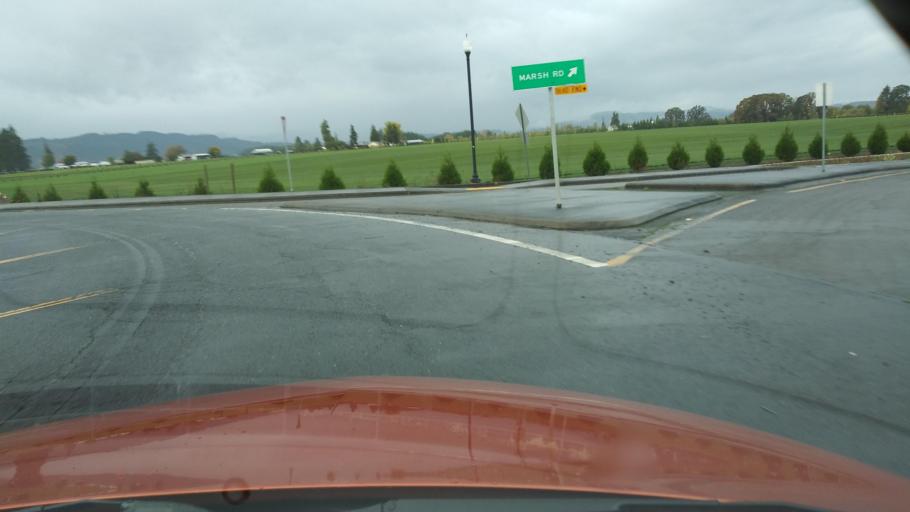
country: US
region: Oregon
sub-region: Washington County
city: Cornelius
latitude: 45.5517
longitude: -123.0732
